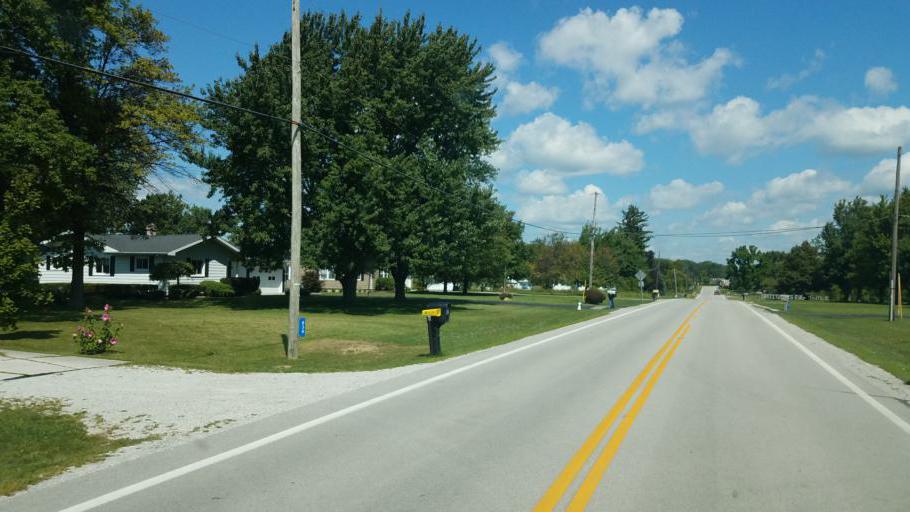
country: US
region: Ohio
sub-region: Seneca County
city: Fostoria
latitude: 41.1349
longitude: -83.3919
